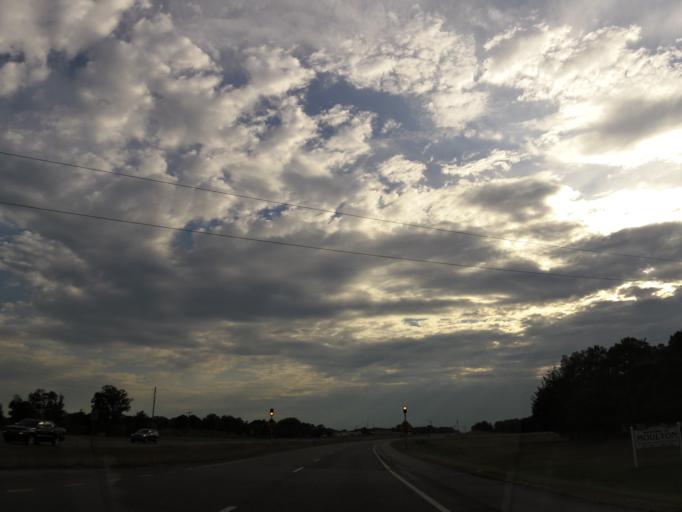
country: US
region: Alabama
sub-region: Lawrence County
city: Moulton
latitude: 34.4948
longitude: -87.2545
